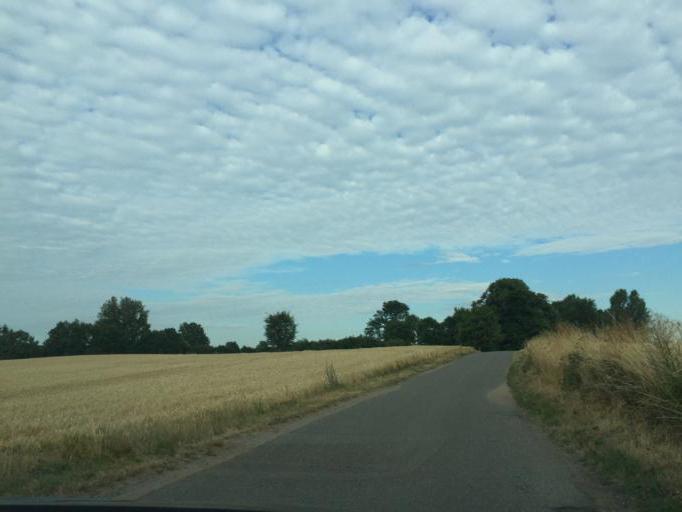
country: DK
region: South Denmark
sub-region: Assens Kommune
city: Assens
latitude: 55.3184
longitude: 9.9674
